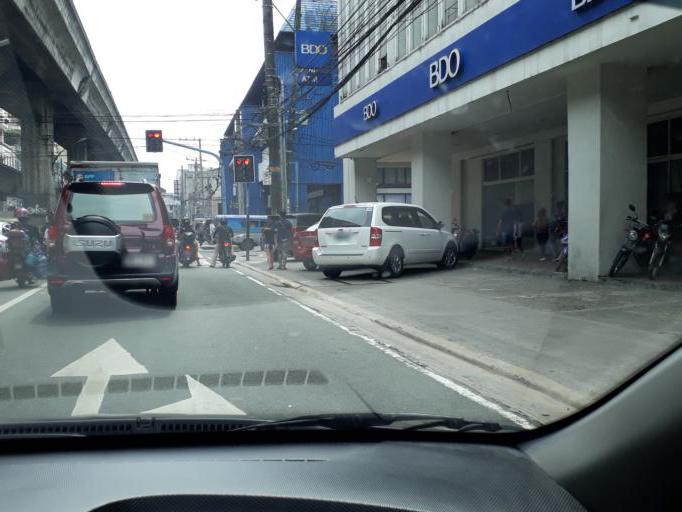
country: PH
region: Metro Manila
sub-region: Quezon City
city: Quezon City
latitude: 14.6242
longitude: 121.0557
